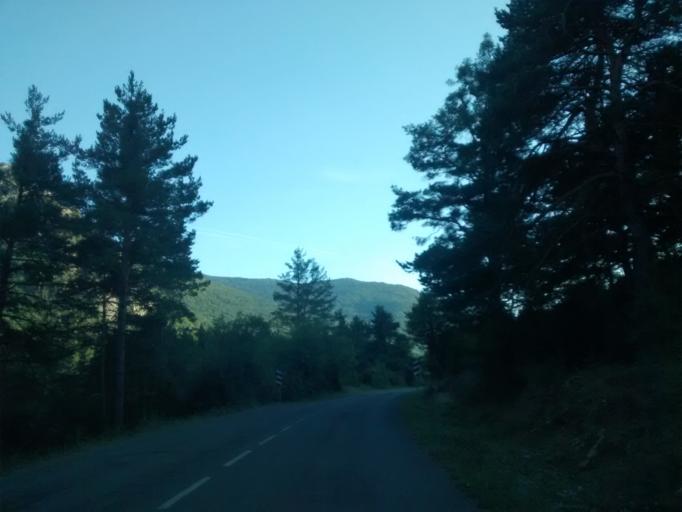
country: ES
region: Aragon
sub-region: Provincia de Huesca
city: Anso
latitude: 42.7925
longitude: -0.7357
